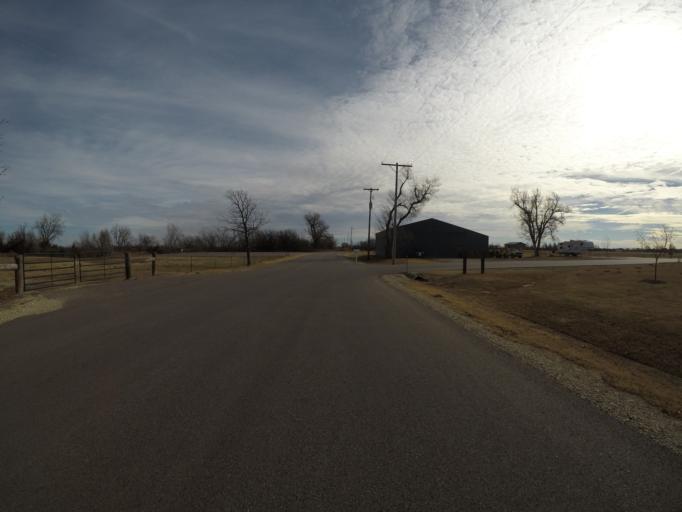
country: US
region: Kansas
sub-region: Reno County
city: Buhler
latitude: 38.1156
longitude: -97.8572
